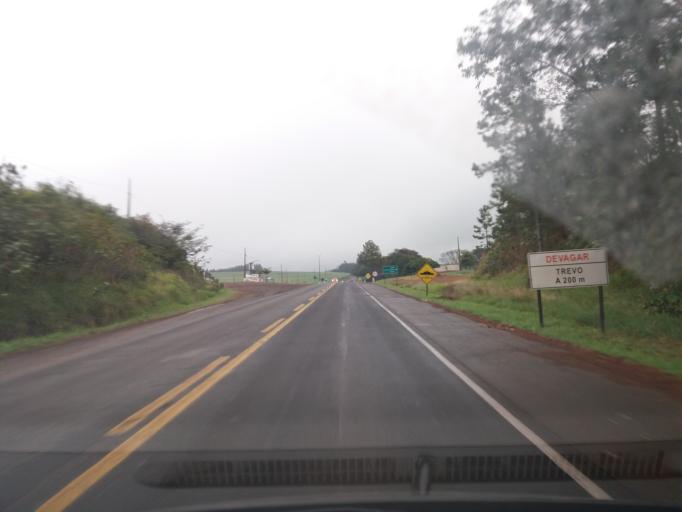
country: BR
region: Parana
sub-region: Ampere
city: Ampere
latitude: -25.9011
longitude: -53.4484
